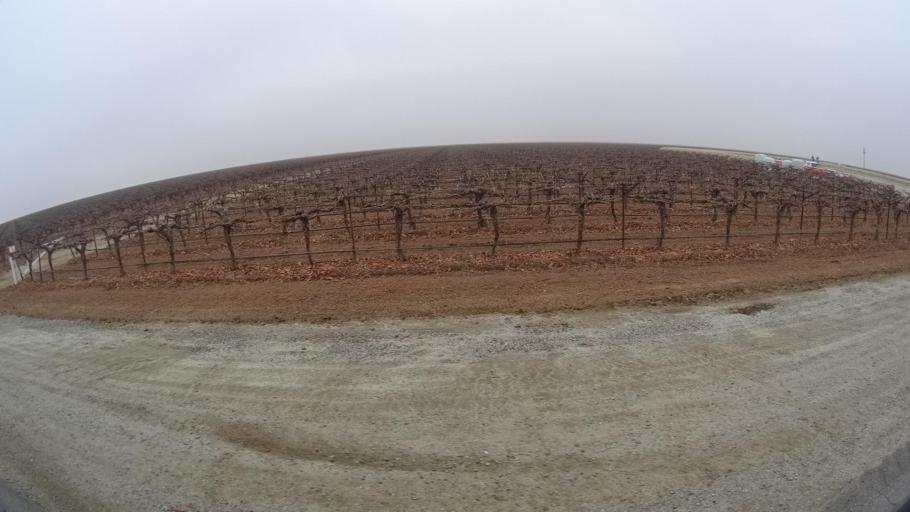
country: US
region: California
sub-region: Kern County
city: Maricopa
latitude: 35.0942
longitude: -119.1740
